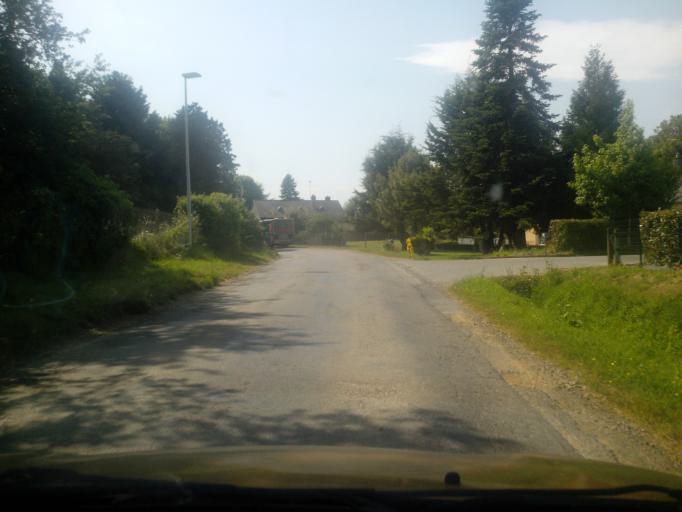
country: FR
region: Brittany
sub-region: Departement d'Ille-et-Vilaine
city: Melesse
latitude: 48.2299
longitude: -1.7018
